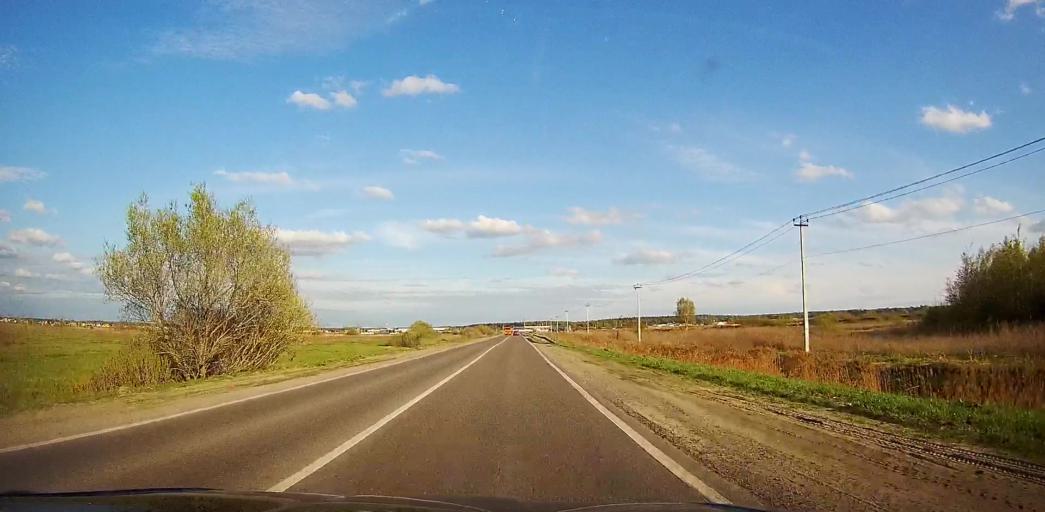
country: RU
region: Moskovskaya
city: Malyshevo
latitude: 55.4912
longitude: 38.3160
